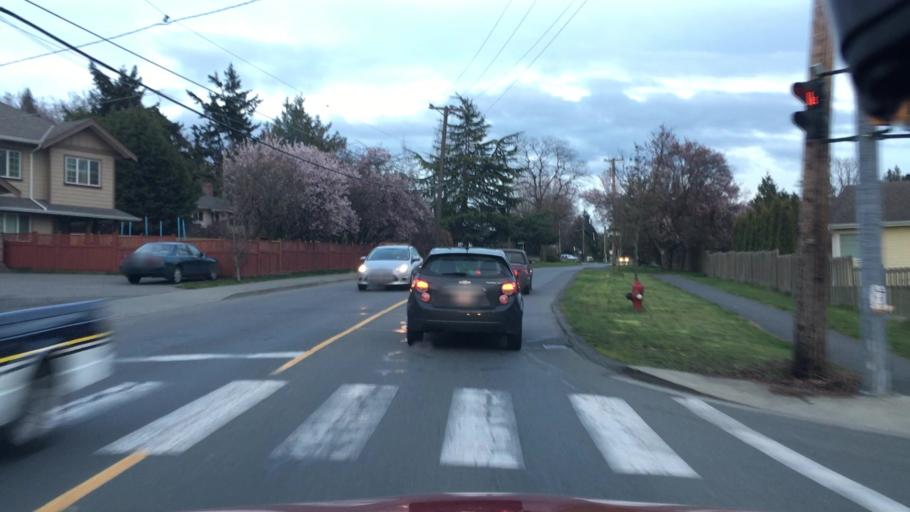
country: CA
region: British Columbia
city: Victoria
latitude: 48.4650
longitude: -123.3444
